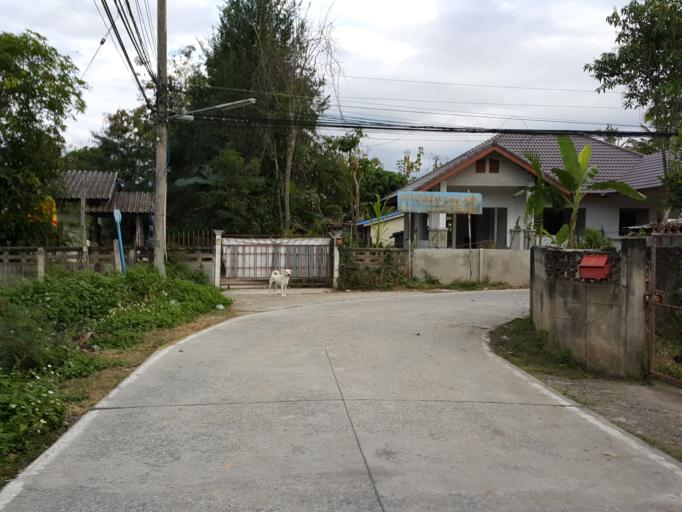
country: TH
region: Chiang Mai
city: San Sai
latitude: 18.8604
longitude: 99.1156
